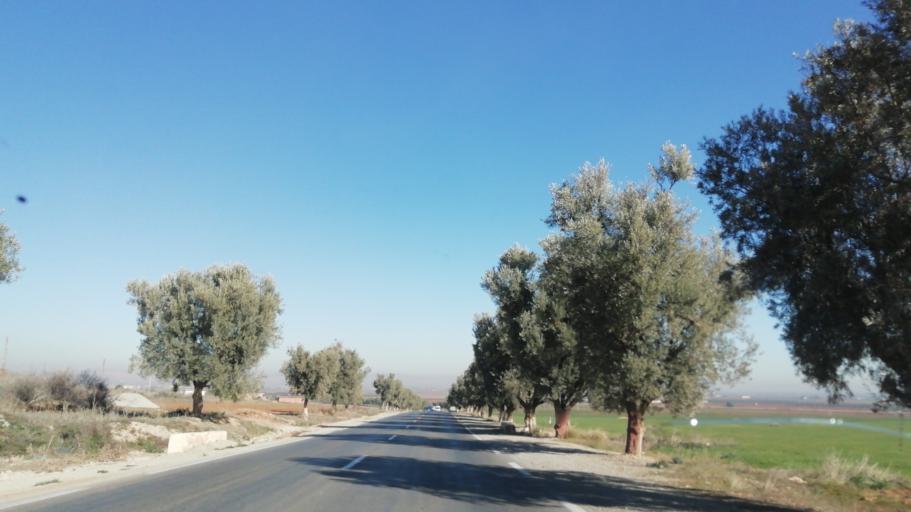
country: DZ
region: Mascara
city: Mascara
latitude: 35.2590
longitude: 0.1270
